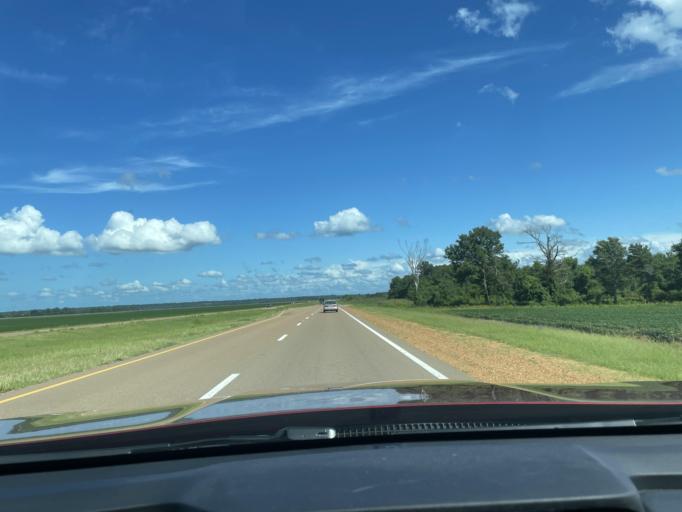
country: US
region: Mississippi
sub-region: Yazoo County
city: Yazoo City
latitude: 32.9572
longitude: -90.4299
